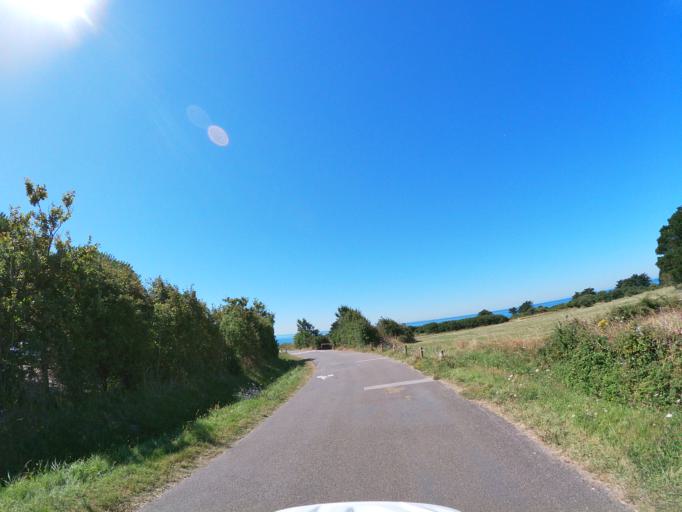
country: FR
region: Pays de la Loire
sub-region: Departement de la Loire-Atlantique
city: La Plaine-sur-Mer
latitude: 47.1224
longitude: -2.1726
